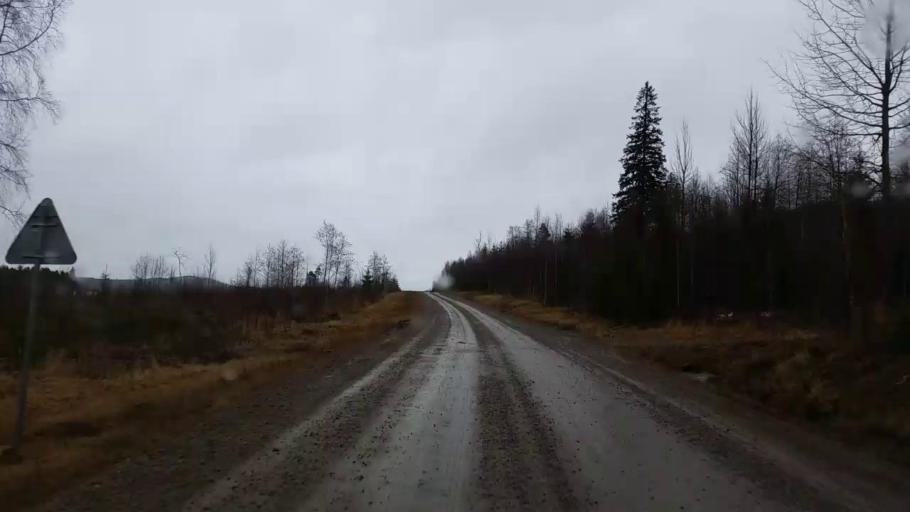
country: SE
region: Gaevleborg
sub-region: Ljusdals Kommun
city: Farila
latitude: 62.0641
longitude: 15.7882
